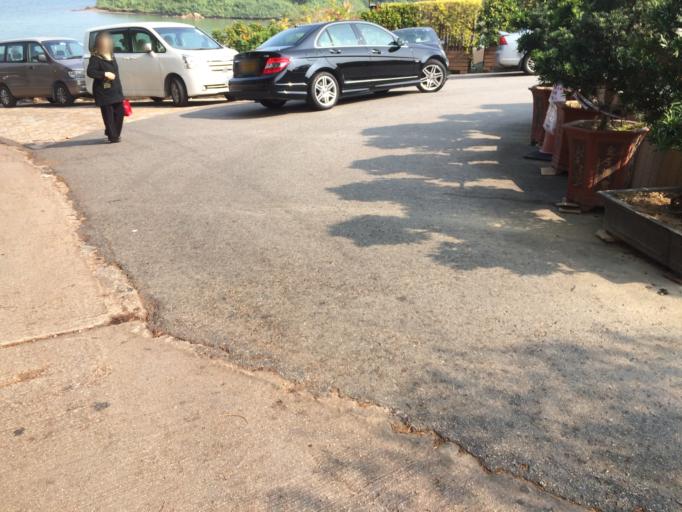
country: HK
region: Tai Po
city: Tai Po
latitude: 22.4568
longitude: 114.2144
